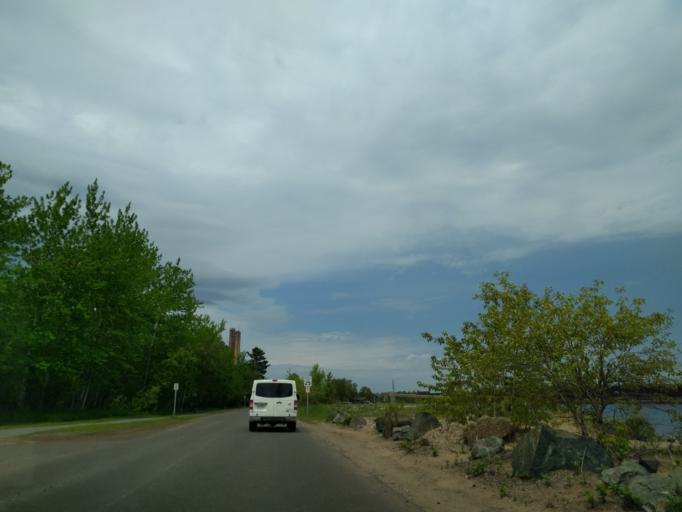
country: US
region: Michigan
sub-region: Marquette County
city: Marquette
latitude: 46.5712
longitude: -87.3933
